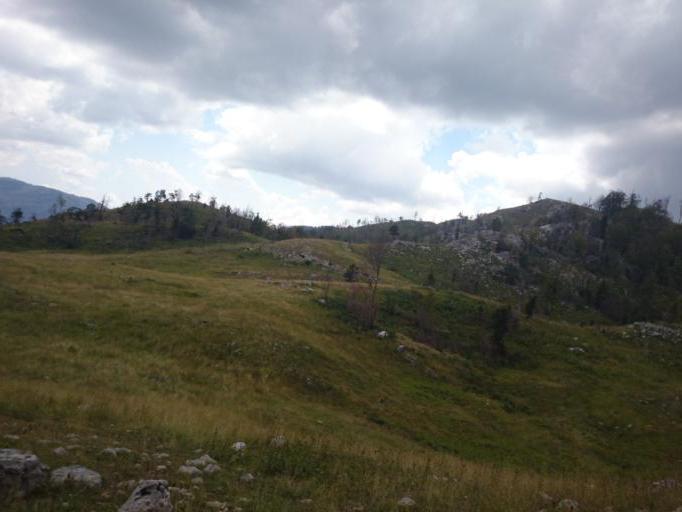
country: AL
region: Lezhe
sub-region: Rrethi i Mirdites
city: Orosh
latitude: 41.8455
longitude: 20.1546
